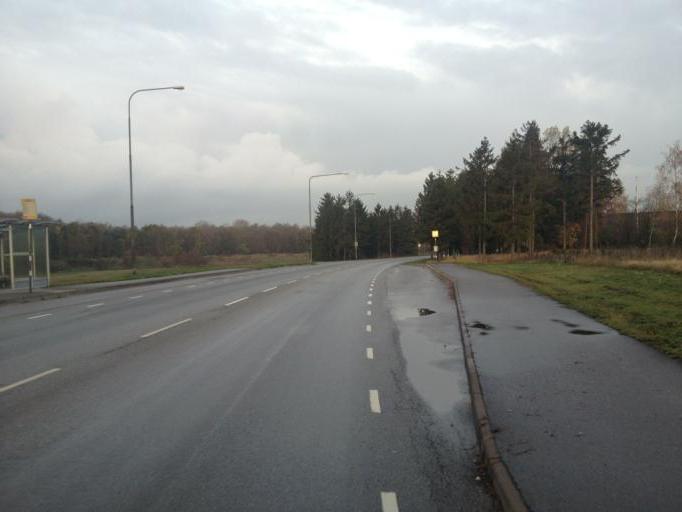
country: SE
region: Skane
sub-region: Kavlinge Kommun
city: Loddekopinge
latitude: 55.7579
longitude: 12.9981
